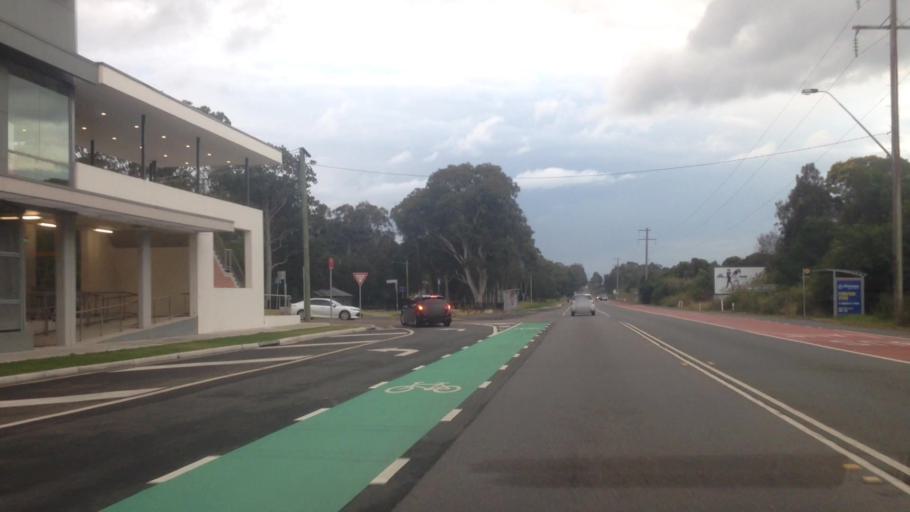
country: AU
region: New South Wales
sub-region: Wyong Shire
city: Chittaway Bay
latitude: -33.2811
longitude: 151.4264
